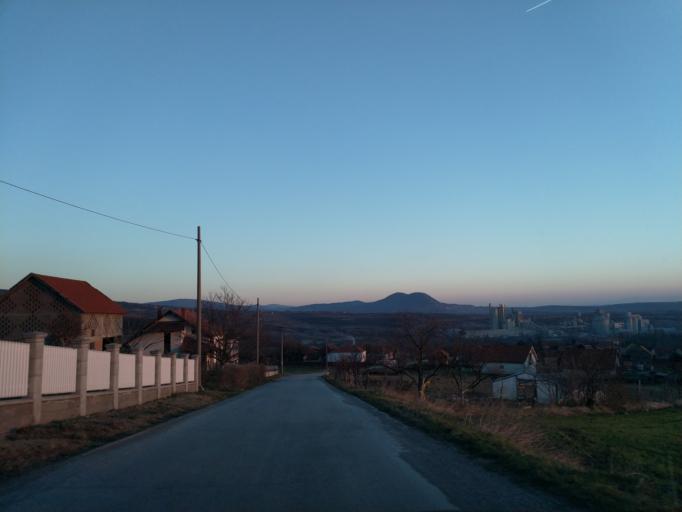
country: RS
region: Central Serbia
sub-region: Pomoravski Okrug
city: Paracin
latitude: 43.9234
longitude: 21.5095
